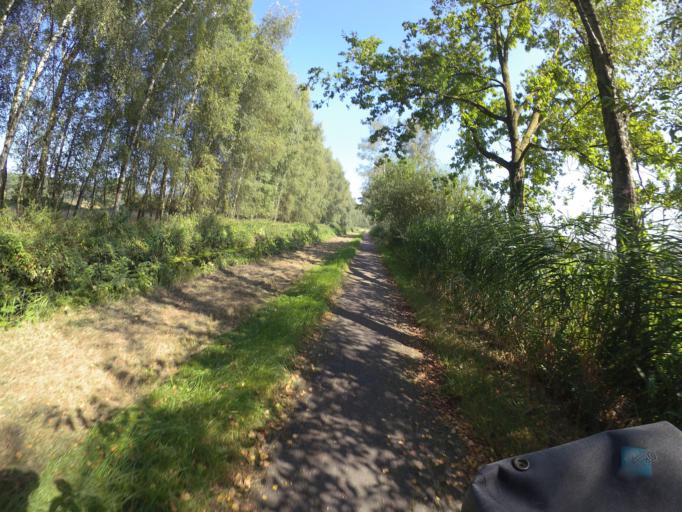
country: NL
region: North Brabant
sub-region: Gemeente Sint Anthonis
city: Sint Anthonis
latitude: 51.5167
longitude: 5.8270
